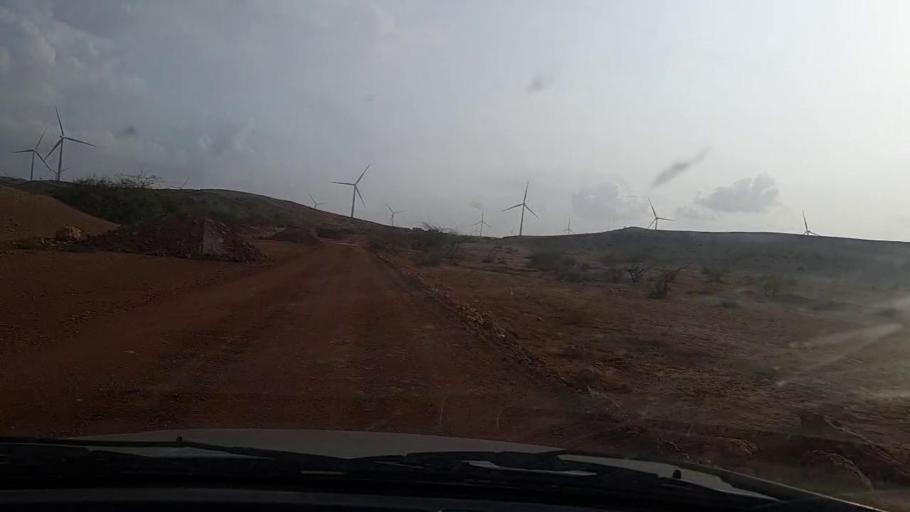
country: PK
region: Sindh
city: Thatta
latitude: 25.0521
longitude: 67.8727
